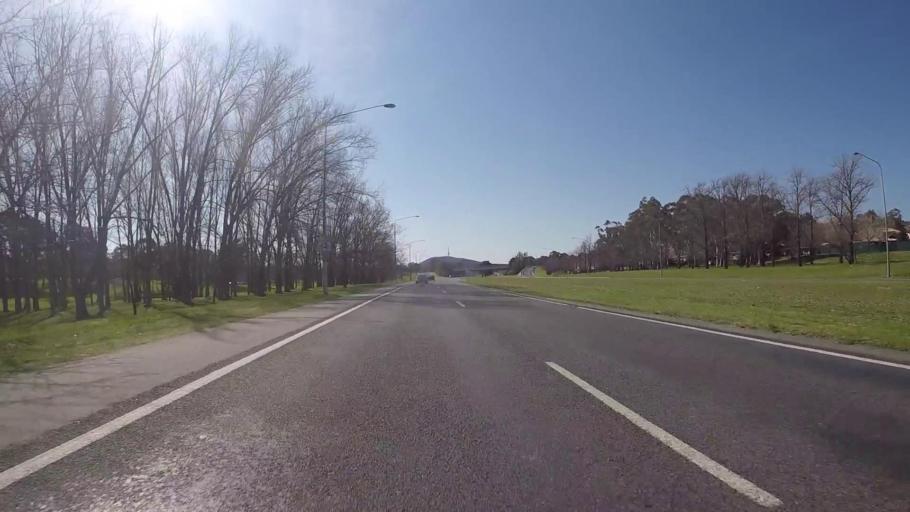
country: AU
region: Australian Capital Territory
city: Forrest
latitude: -35.3301
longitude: 149.0861
